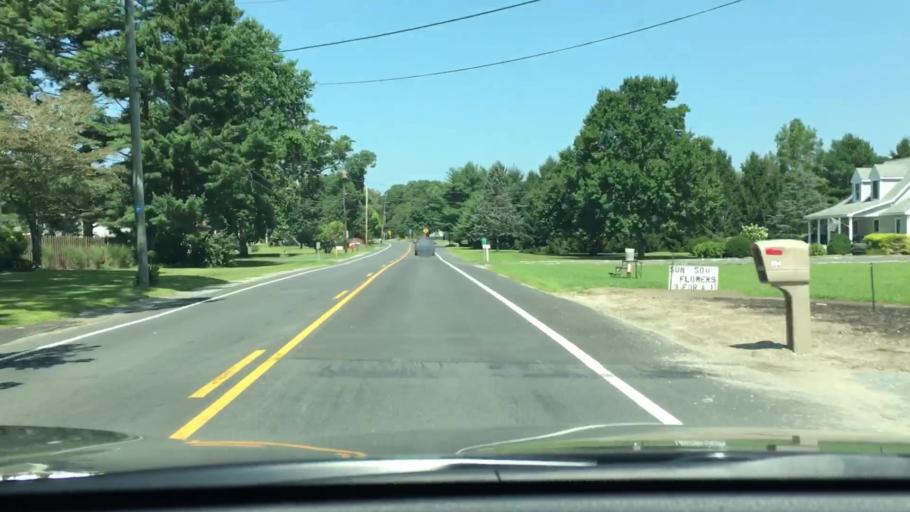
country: US
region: New Jersey
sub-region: Cape May County
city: Woodbine
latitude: 39.2662
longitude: -74.8639
